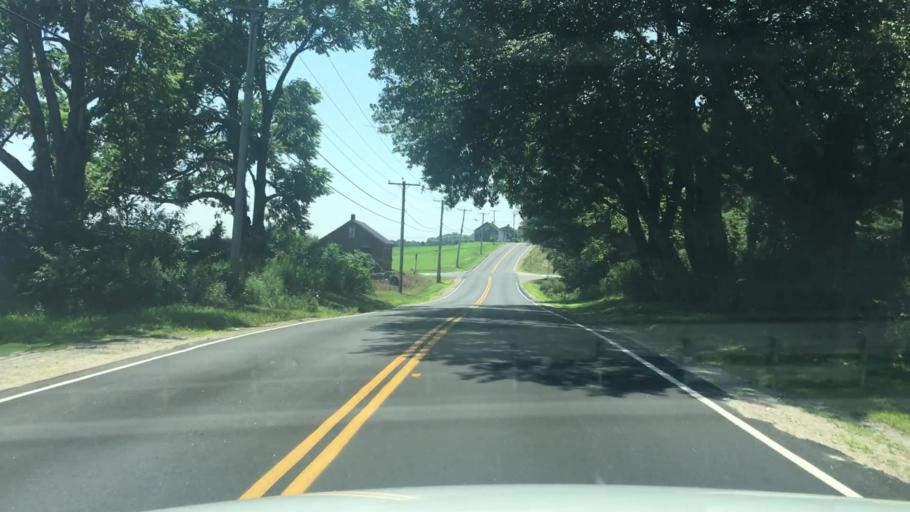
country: US
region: Maine
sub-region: Cumberland County
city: Cumberland Center
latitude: 43.7791
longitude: -70.2594
